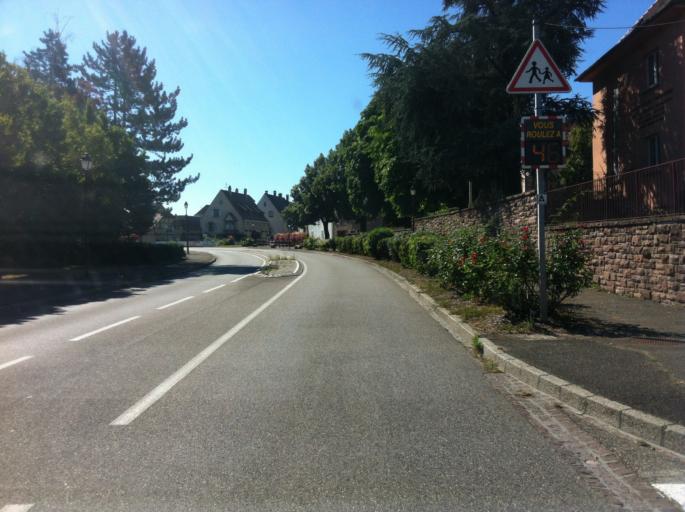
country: FR
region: Alsace
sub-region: Departement du Haut-Rhin
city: Ammerschwihr
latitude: 48.1286
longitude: 7.2818
